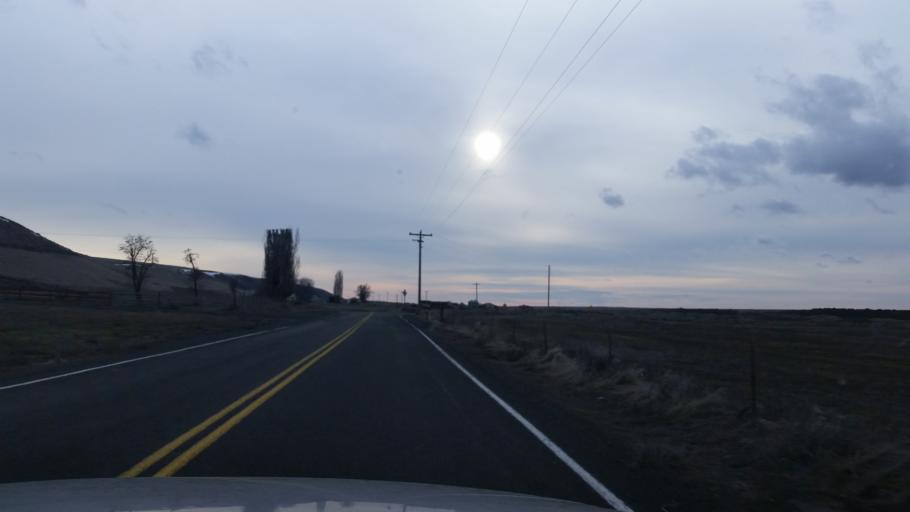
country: US
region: Washington
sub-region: Adams County
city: Ritzville
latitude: 47.1853
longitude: -117.9275
